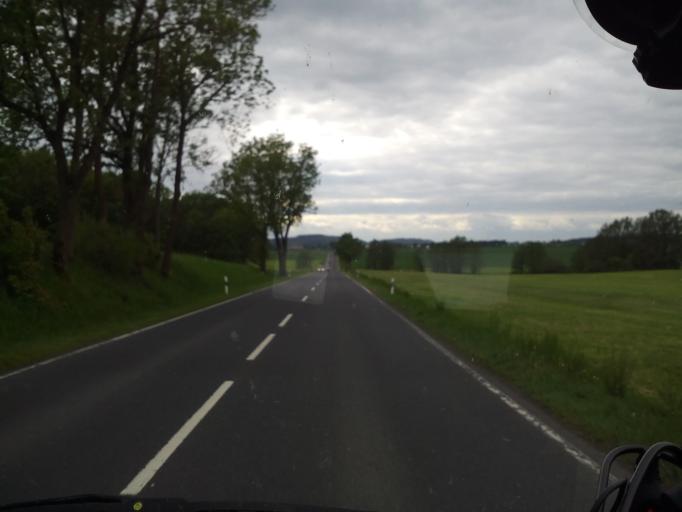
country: DE
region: Thuringia
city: Veilsdorf
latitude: 50.4162
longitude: 10.7994
